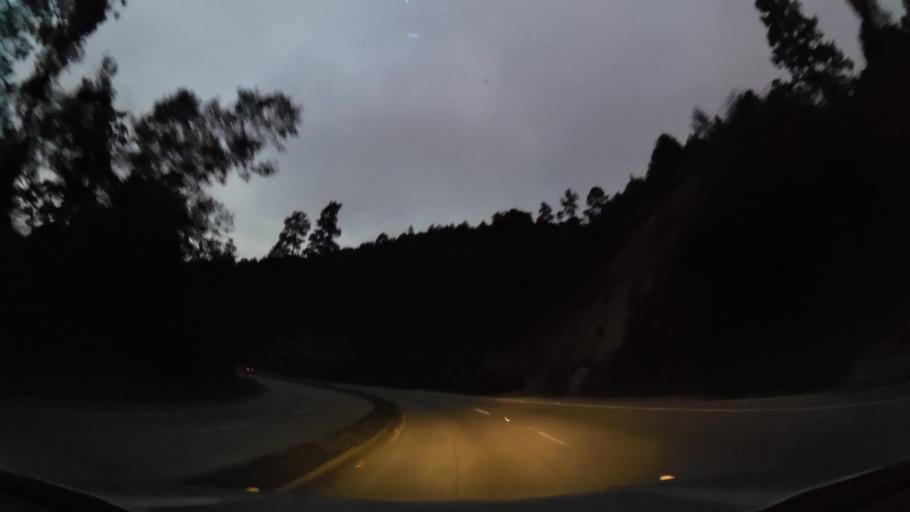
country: GT
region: Chimaltenango
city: Santa Apolonia
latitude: 14.8094
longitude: -90.9964
